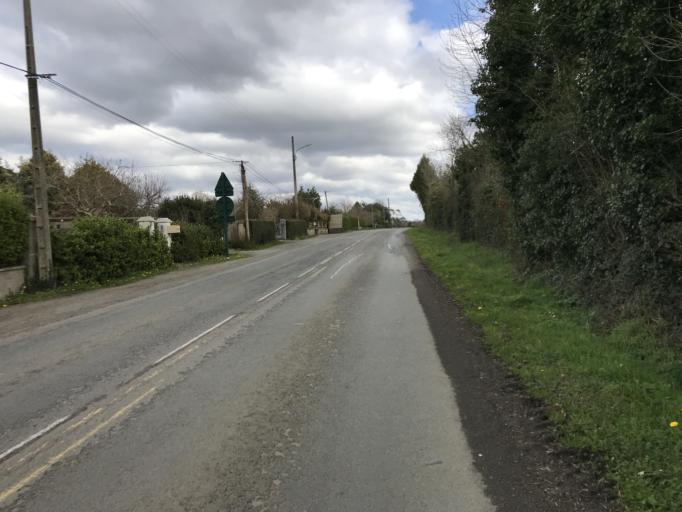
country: FR
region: Brittany
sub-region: Departement du Finistere
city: Hopital-Camfrout
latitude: 48.3256
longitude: -4.2321
